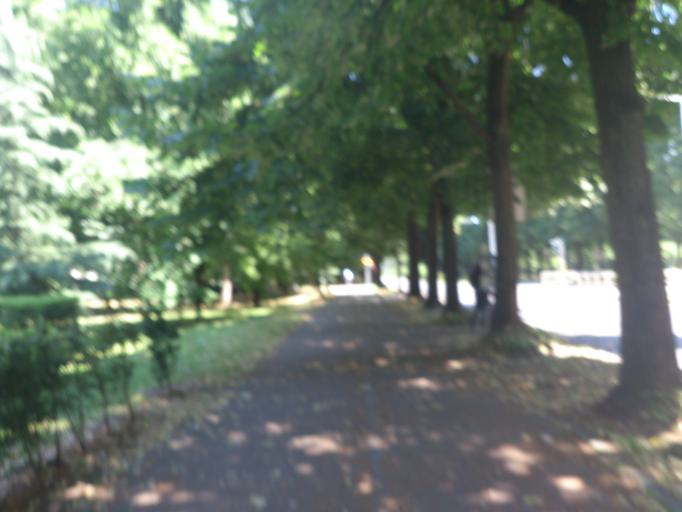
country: IT
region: Lombardy
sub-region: Citta metropolitana di Milano
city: San Donato Milanese
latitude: 45.4252
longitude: 9.2659
